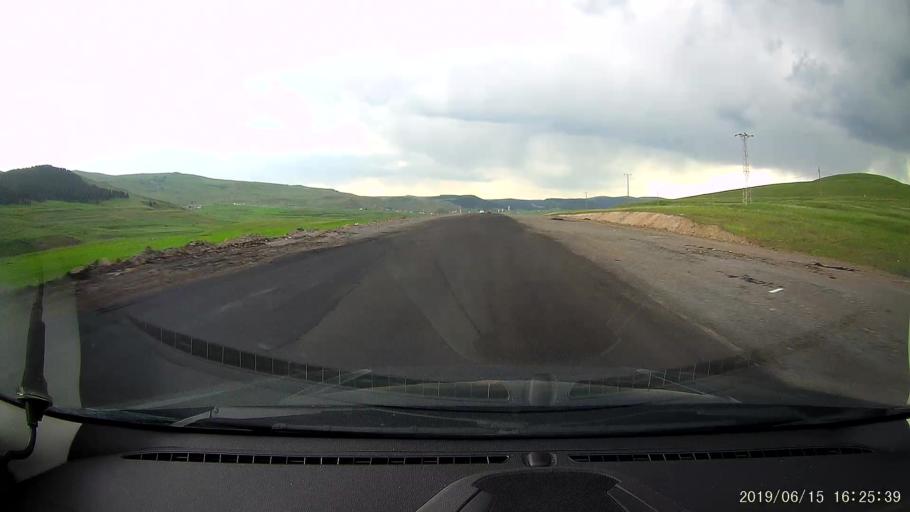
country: TR
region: Ardahan
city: Hanak
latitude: 41.1510
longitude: 42.8678
